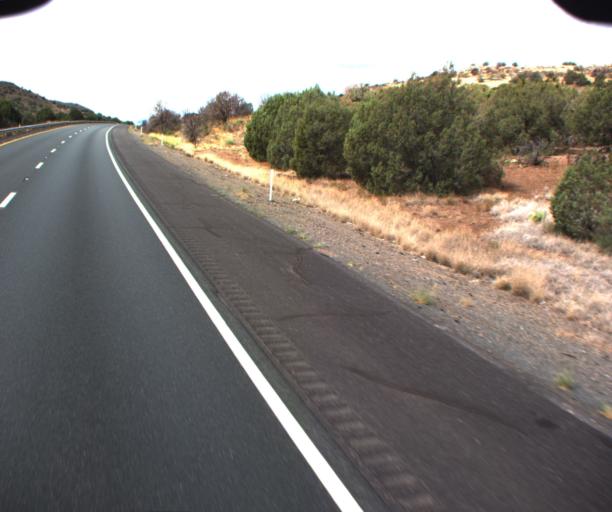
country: US
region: Arizona
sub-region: Yavapai County
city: Camp Verde
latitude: 34.4917
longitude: -112.0075
